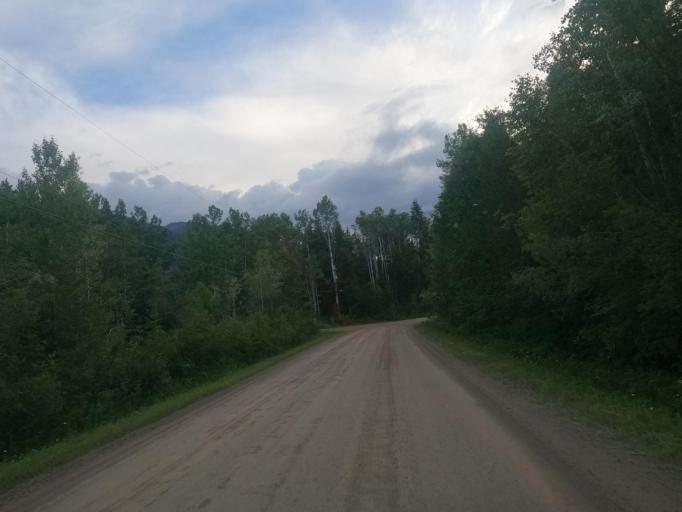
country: CA
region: British Columbia
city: Golden
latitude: 51.4451
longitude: -117.0366
